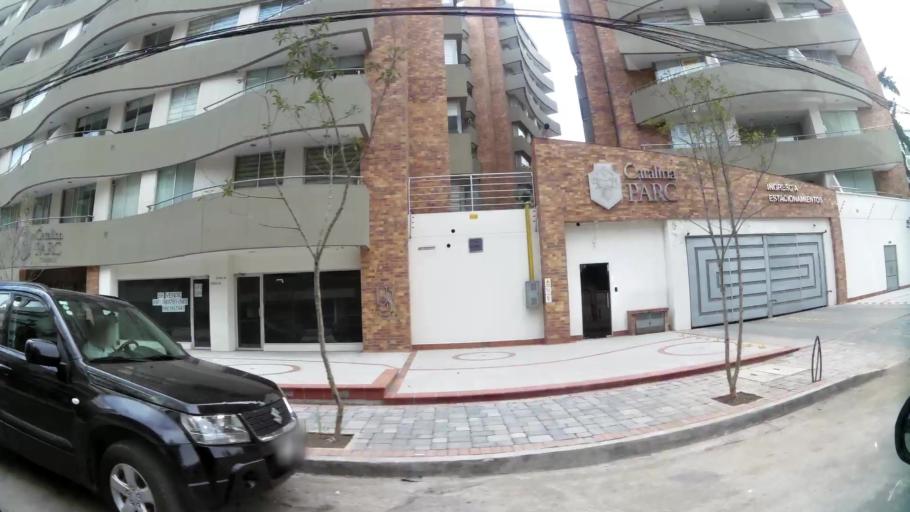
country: EC
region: Pichincha
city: Quito
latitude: -0.1838
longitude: -78.4771
